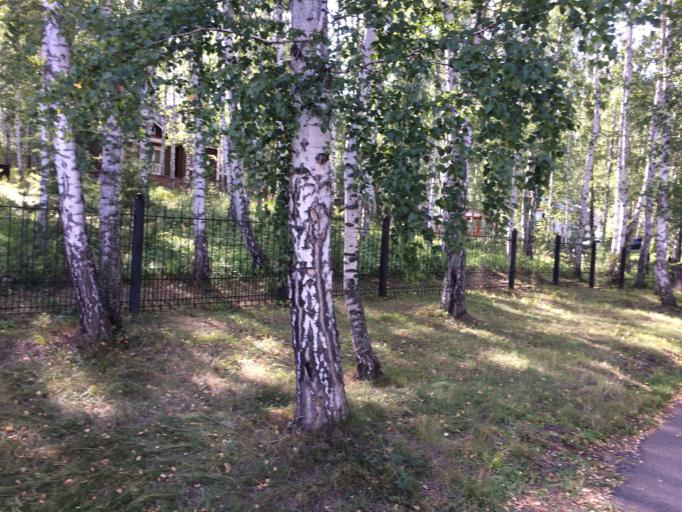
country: RU
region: Bashkortostan
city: Abzakovo
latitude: 53.8121
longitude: 58.6270
